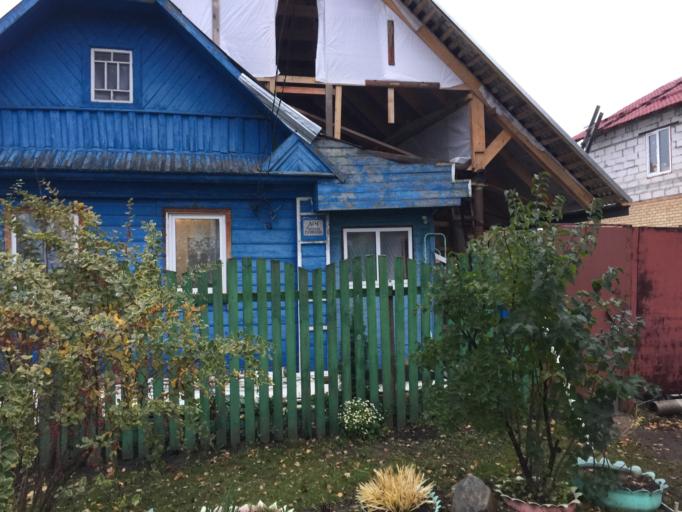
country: RU
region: Jaroslavl
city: Yaroslavl
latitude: 57.7207
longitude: 39.7728
